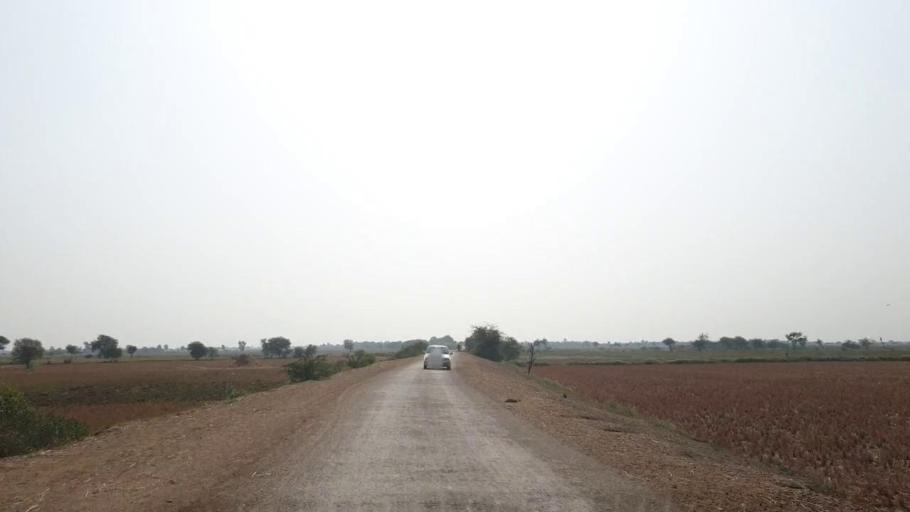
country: PK
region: Sindh
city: Matli
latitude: 24.9722
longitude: 68.5868
